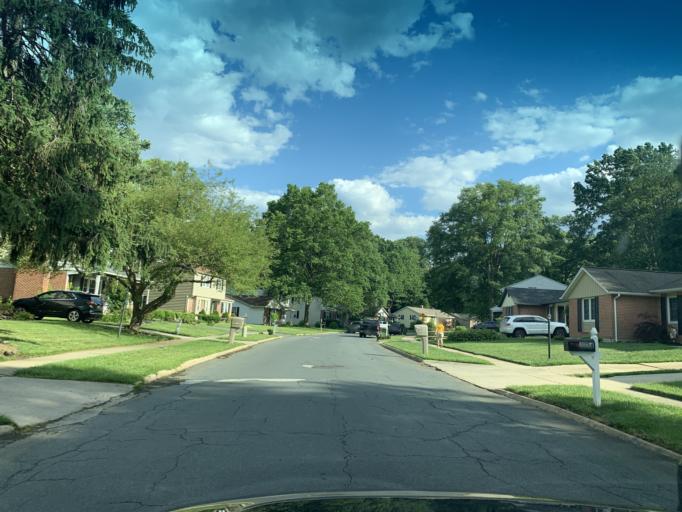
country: US
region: Maryland
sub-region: Harford County
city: Bel Air North
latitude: 39.5522
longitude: -76.3701
